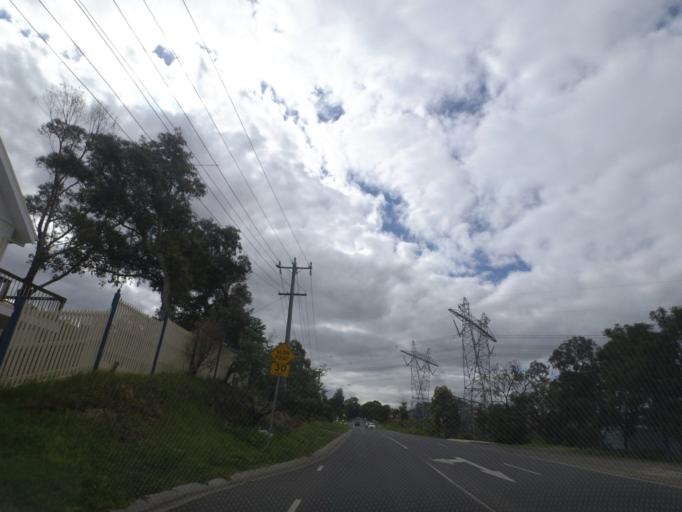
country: AU
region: Victoria
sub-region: Nillumbik
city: Diamond Creek
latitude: -37.6656
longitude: 145.1640
